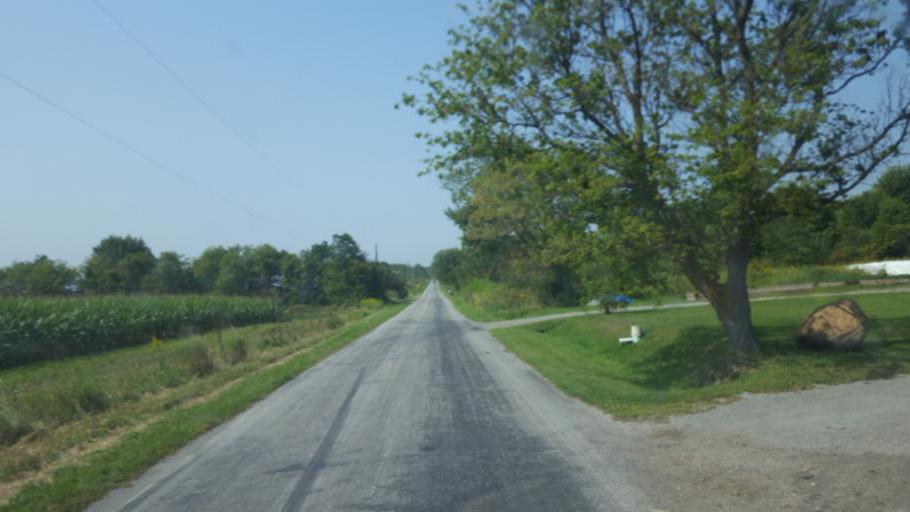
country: US
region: Ohio
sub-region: Ashtabula County
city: Orwell
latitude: 41.4891
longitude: -80.8859
